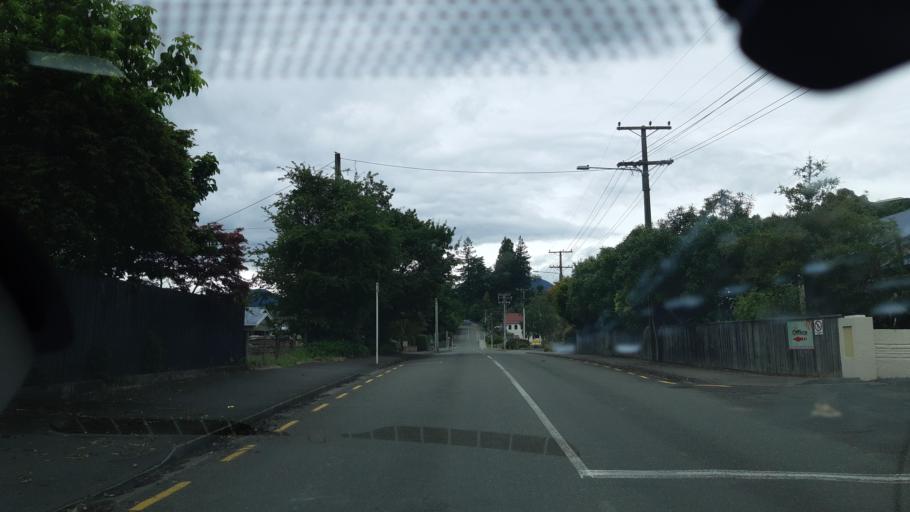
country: NZ
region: Tasman
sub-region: Tasman District
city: Wakefield
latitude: -41.4072
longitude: 173.0443
